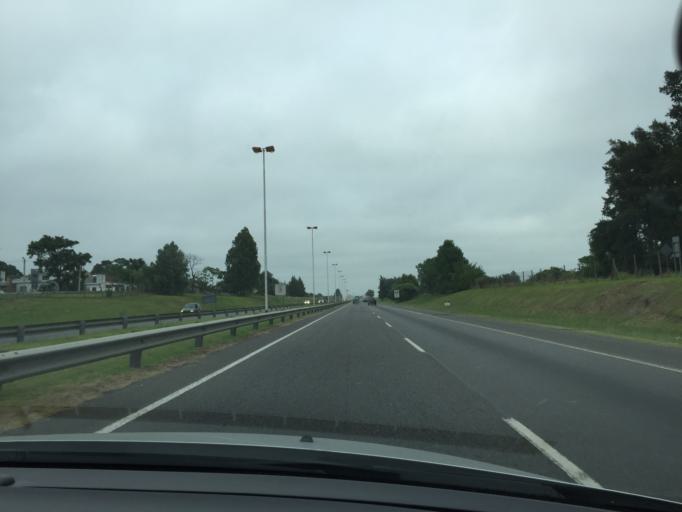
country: AR
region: Buenos Aires
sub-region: Partido de Ezeiza
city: Ezeiza
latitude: -34.8357
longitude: -58.5160
